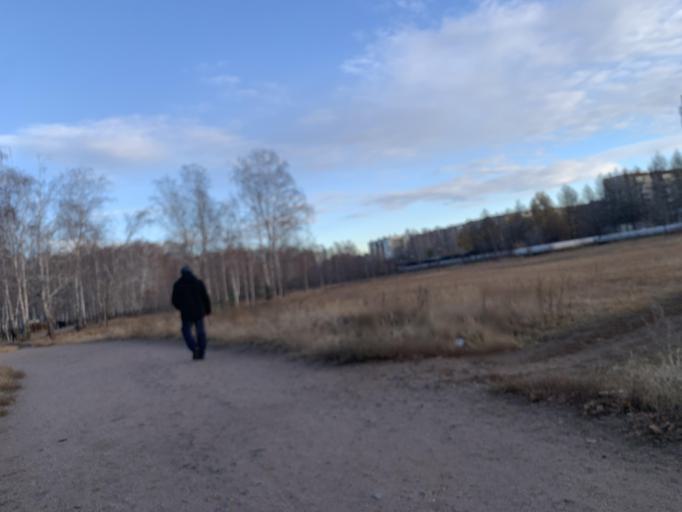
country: RU
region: Chelyabinsk
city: Roshchino
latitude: 55.2006
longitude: 61.3059
